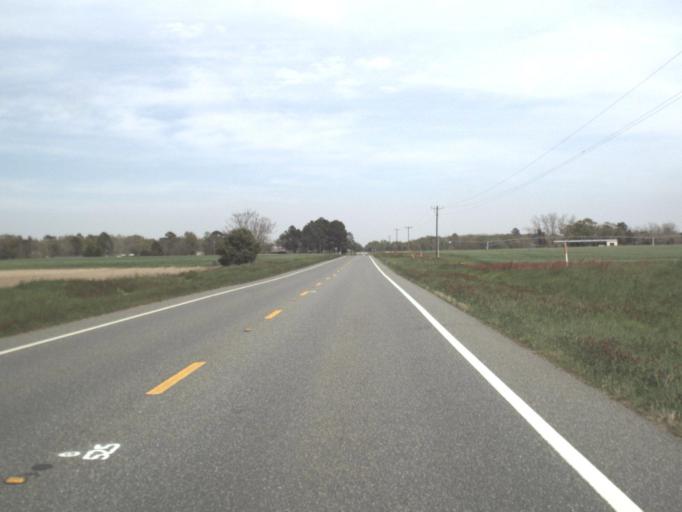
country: US
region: Florida
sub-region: Jackson County
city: Malone
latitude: 30.9501
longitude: -85.2462
